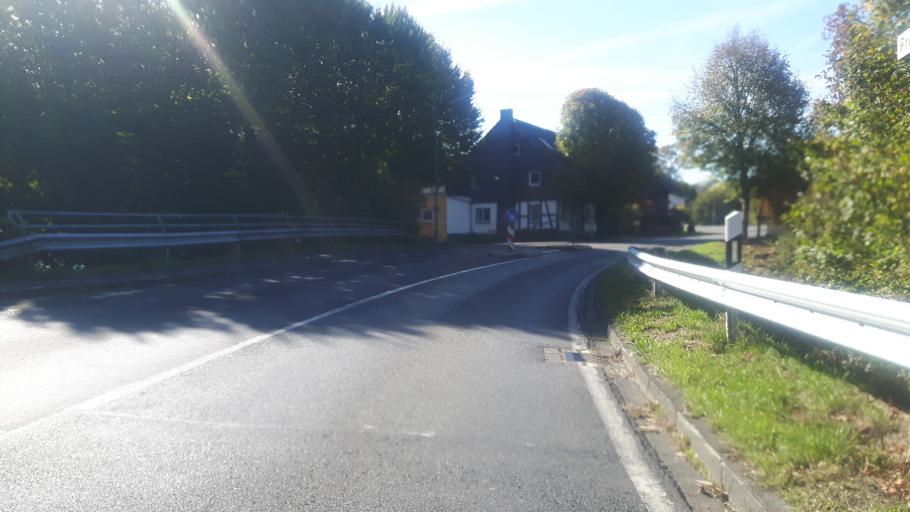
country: DE
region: Rheinland-Pfalz
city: Furthen
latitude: 50.7887
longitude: 7.6238
